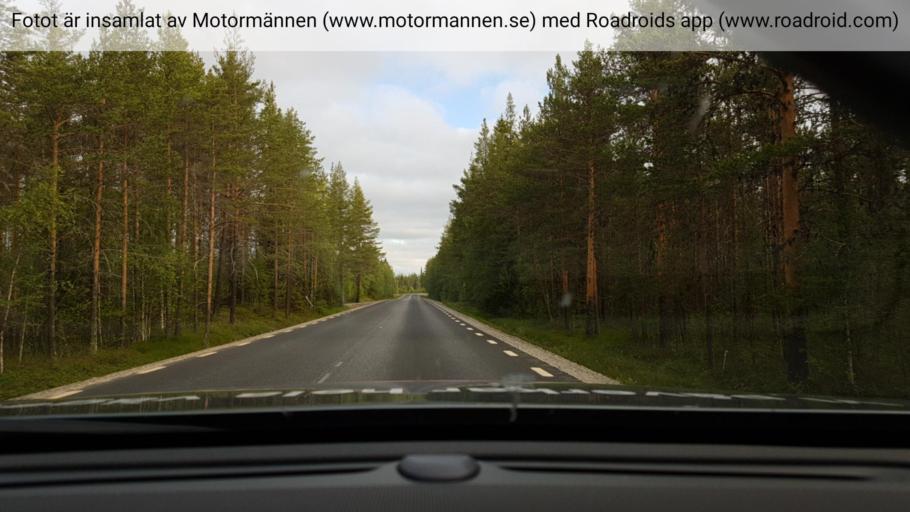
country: SE
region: Vaesterbotten
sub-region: Norsjo Kommun
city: Norsjoe
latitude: 64.4712
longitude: 19.3264
